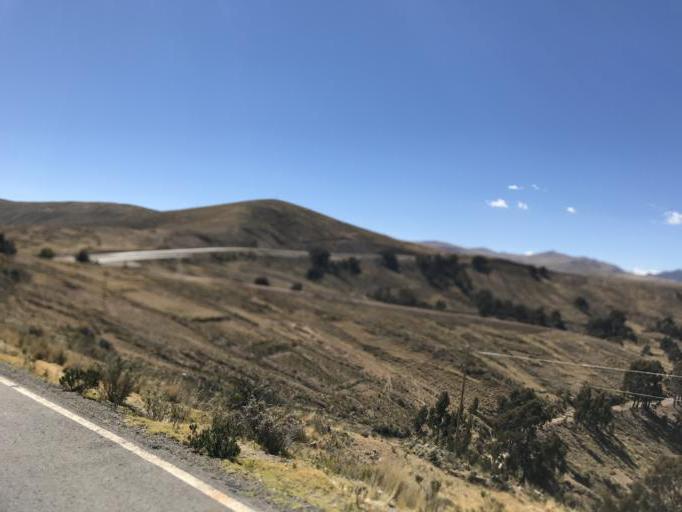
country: BO
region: La Paz
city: San Pablo
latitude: -16.2063
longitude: -68.8322
